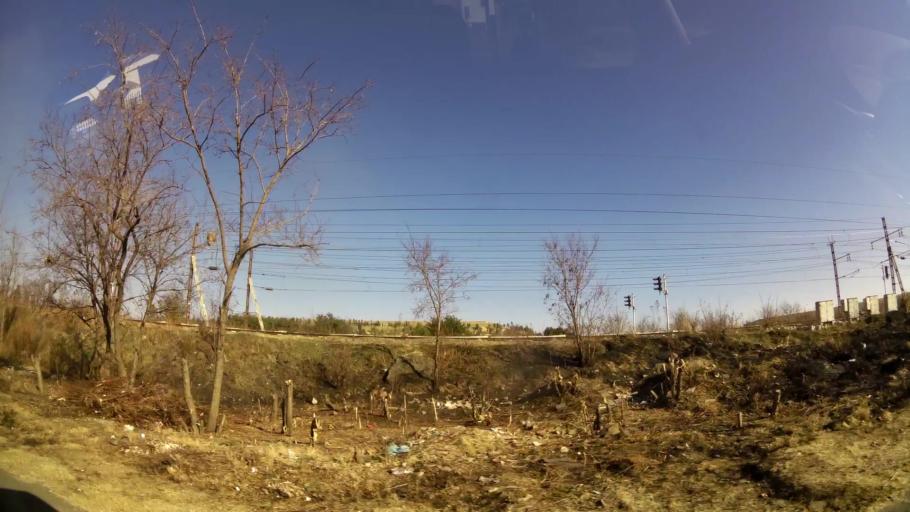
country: ZA
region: Gauteng
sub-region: City of Johannesburg Metropolitan Municipality
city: Johannesburg
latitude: -26.2152
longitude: 27.9715
